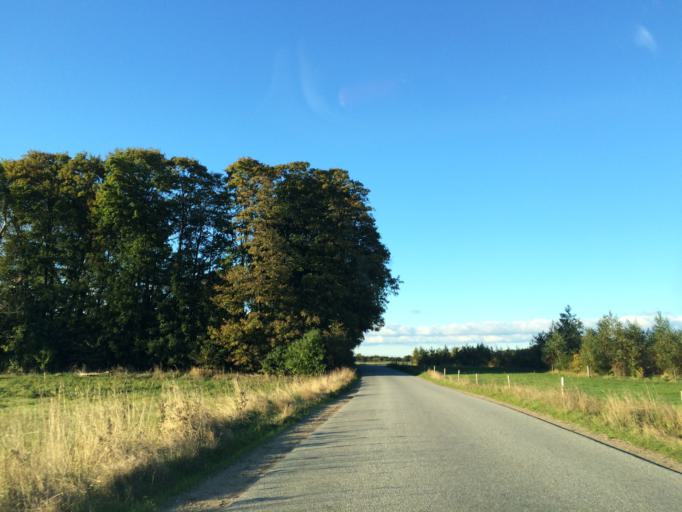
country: DK
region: Central Jutland
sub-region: Silkeborg Kommune
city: Svejbaek
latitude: 56.1785
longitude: 9.6926
